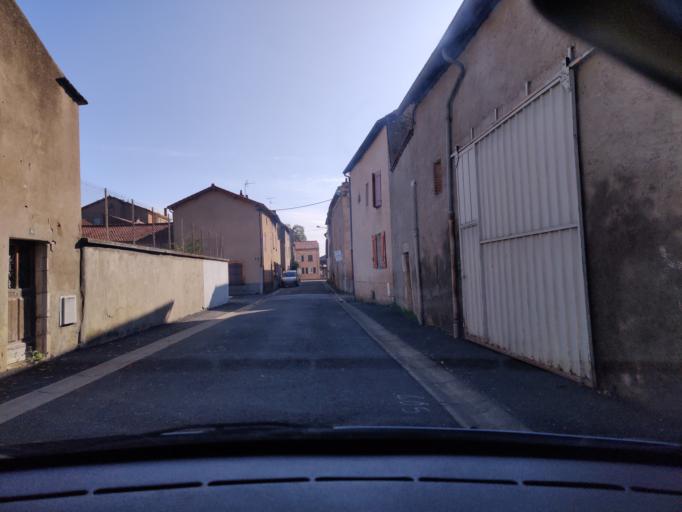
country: FR
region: Auvergne
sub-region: Departement du Puy-de-Dome
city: Aigueperse
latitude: 46.0261
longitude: 3.2039
